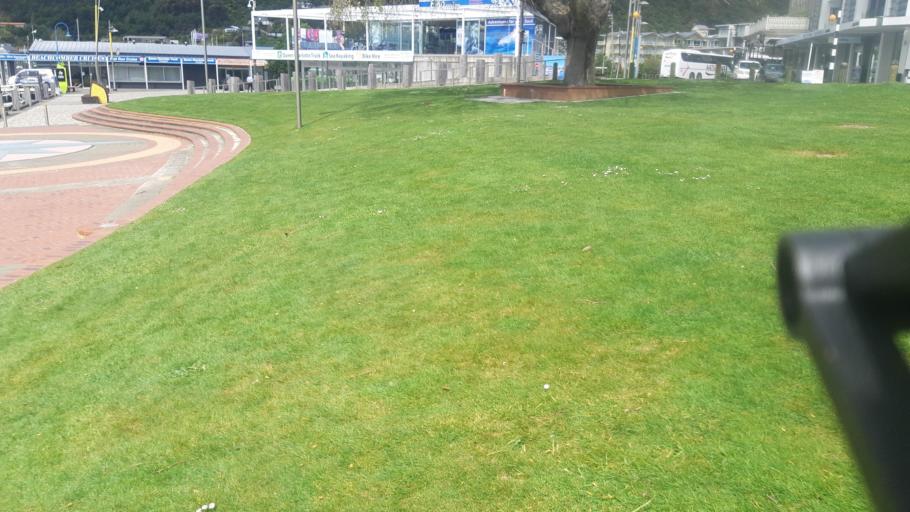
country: NZ
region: Marlborough
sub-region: Marlborough District
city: Picton
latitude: -41.2885
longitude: 174.0075
